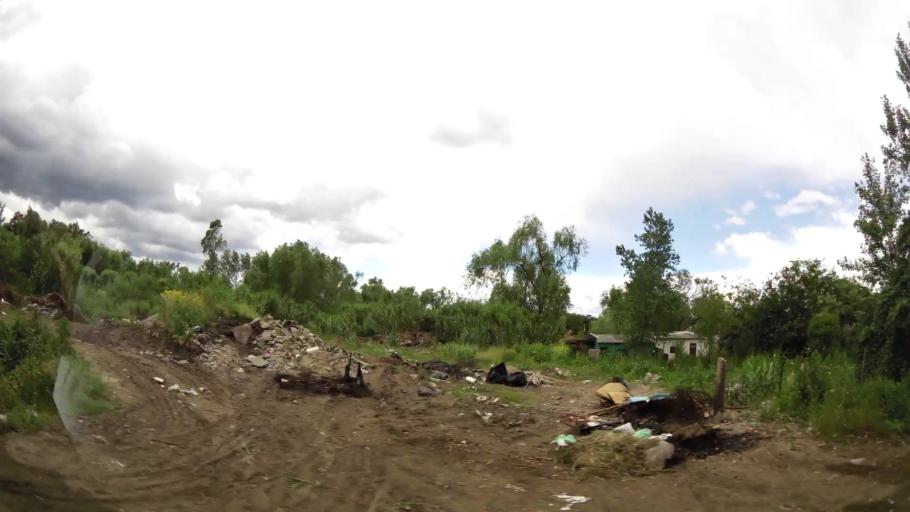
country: UY
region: Canelones
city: Toledo
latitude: -34.8017
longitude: -56.1295
